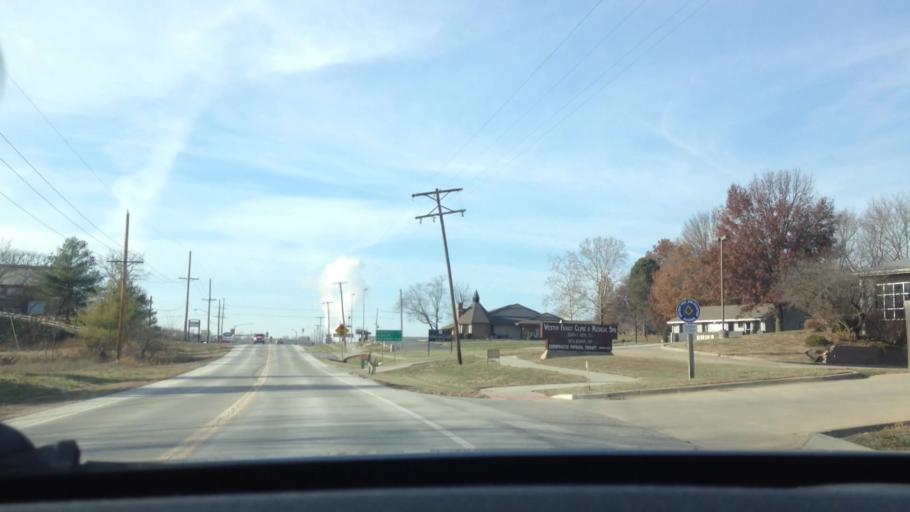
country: US
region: Missouri
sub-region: Platte County
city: Weston
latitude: 39.4219
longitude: -94.8971
